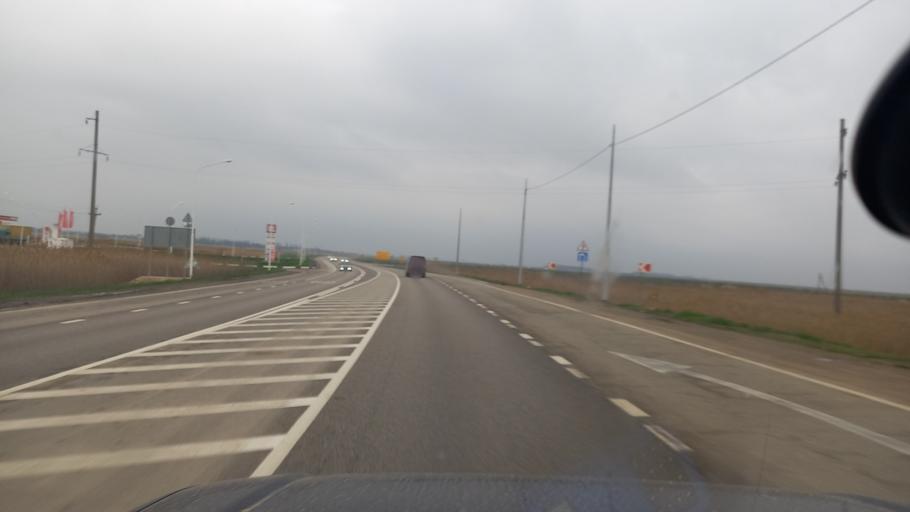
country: RU
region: Krasnodarskiy
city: Novomyshastovskaya
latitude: 45.1819
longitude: 38.5649
